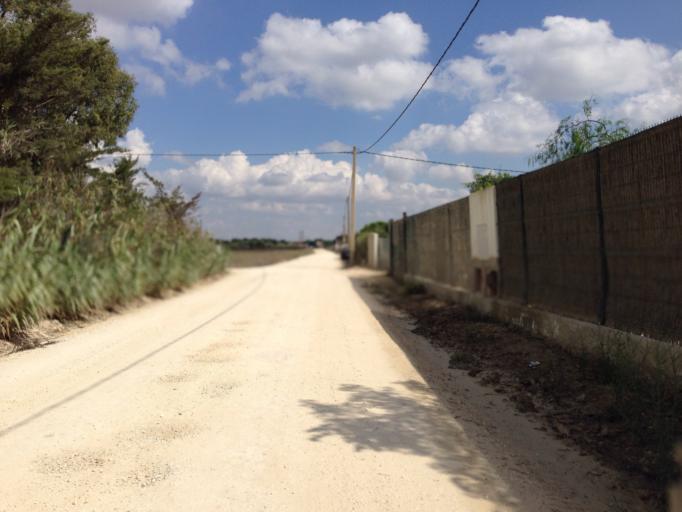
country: ES
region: Andalusia
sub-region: Provincia de Cadiz
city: Conil de la Frontera
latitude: 36.2479
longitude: -6.0712
